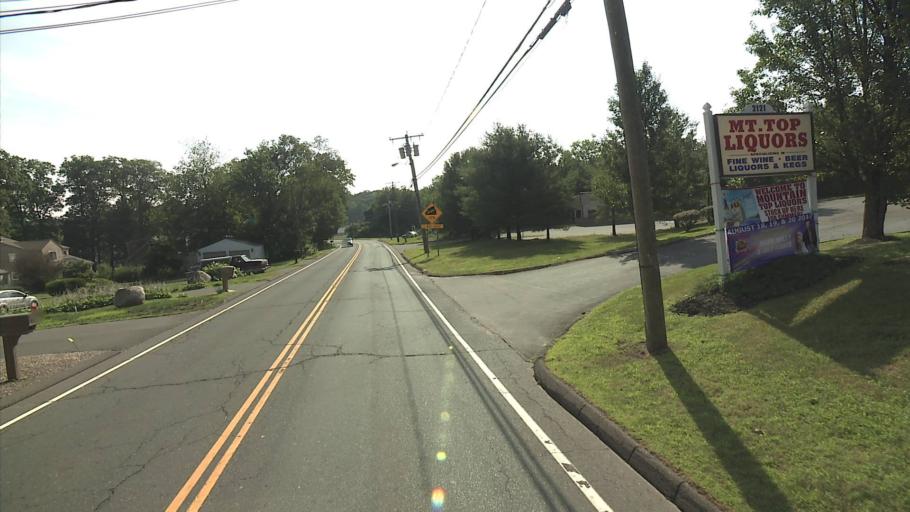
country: US
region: Connecticut
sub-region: New Haven County
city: Wolcott
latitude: 41.5557
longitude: -72.9536
